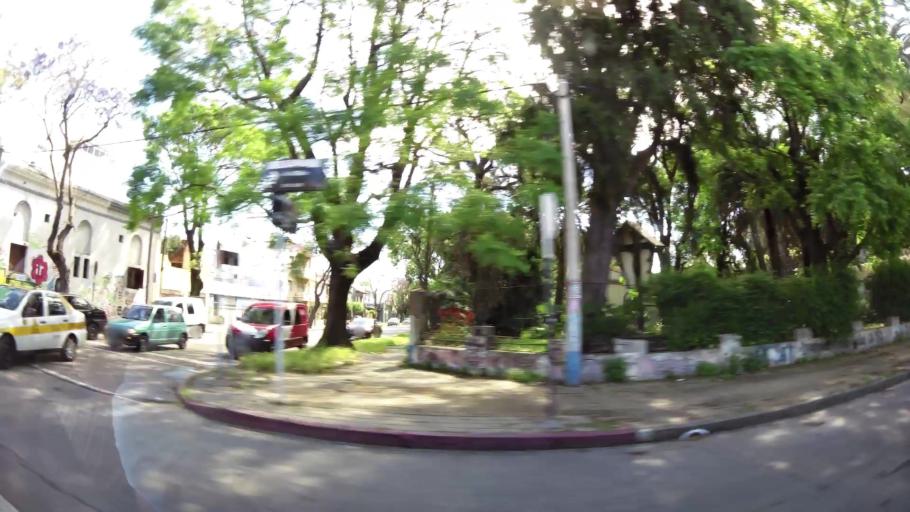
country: UY
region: Montevideo
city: Montevideo
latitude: -34.8674
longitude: -56.1922
